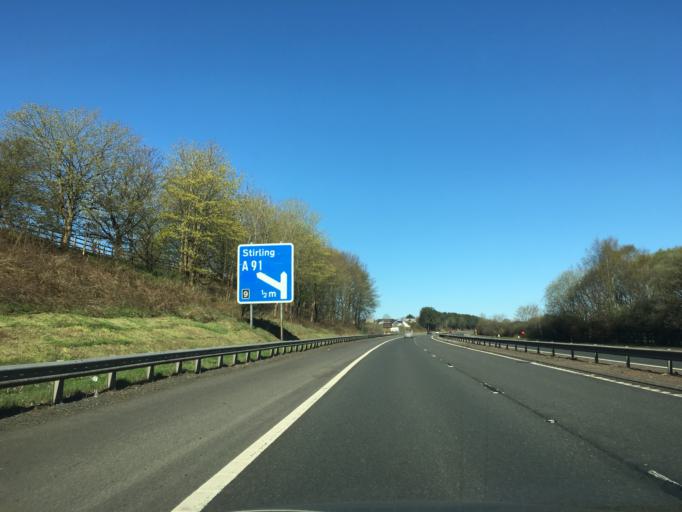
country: GB
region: Scotland
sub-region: Stirling
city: Plean
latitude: 56.0699
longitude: -3.8976
